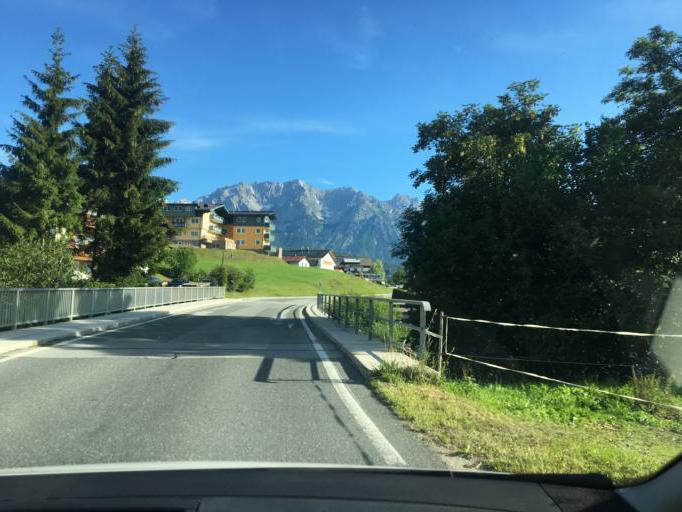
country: AT
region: Styria
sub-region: Politischer Bezirk Liezen
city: Schladming
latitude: 47.3793
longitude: 13.6723
